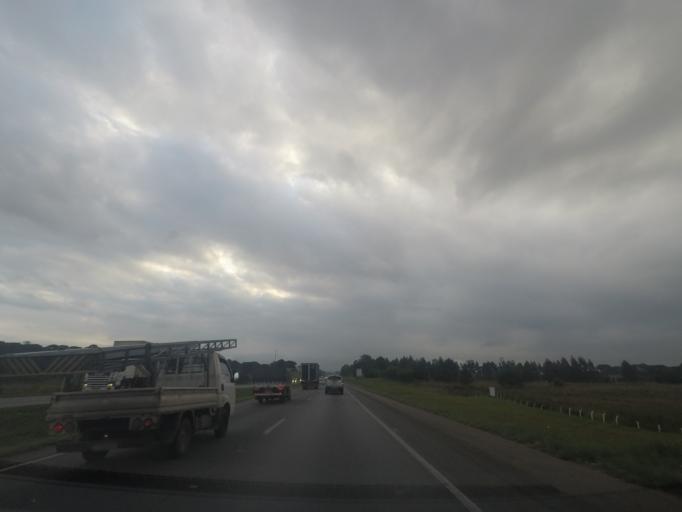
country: BR
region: Parana
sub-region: Sao Jose Dos Pinhais
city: Sao Jose dos Pinhais
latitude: -25.5661
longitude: -49.2427
